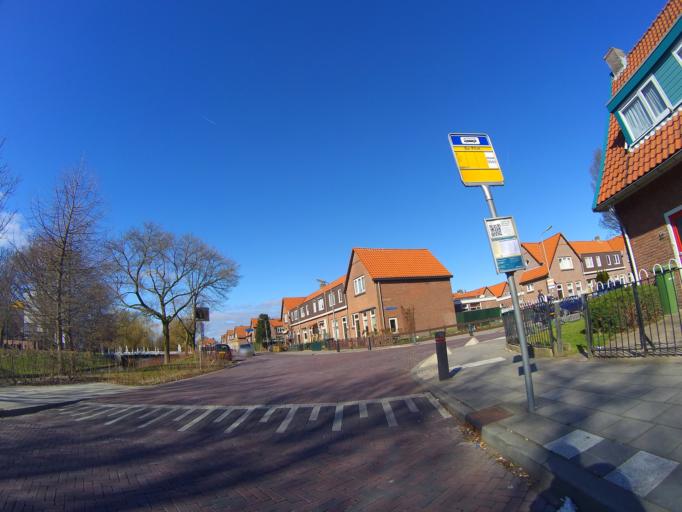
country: NL
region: Utrecht
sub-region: Gemeente Amersfoort
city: Amersfoort
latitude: 52.1604
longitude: 5.3946
